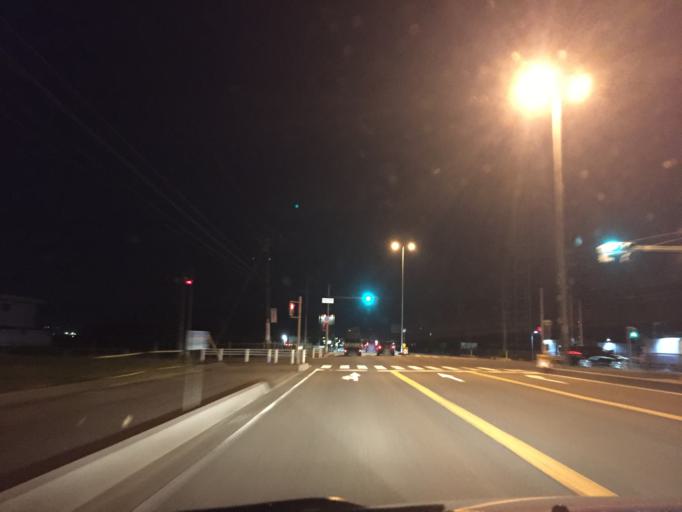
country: JP
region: Gifu
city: Ogaki
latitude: 35.2884
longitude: 136.6047
